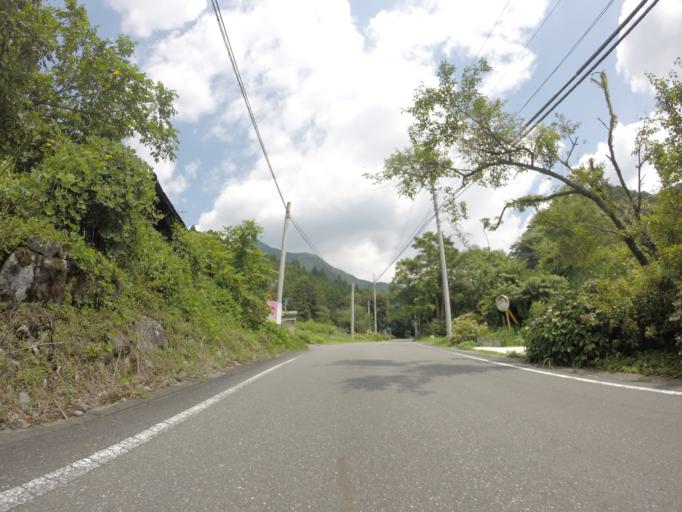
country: JP
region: Shizuoka
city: Fujinomiya
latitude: 35.2751
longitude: 138.3279
